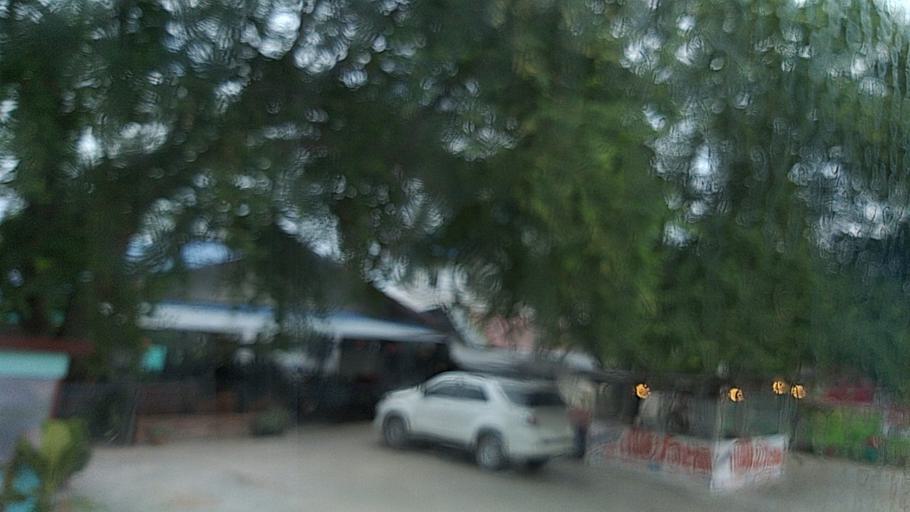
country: TH
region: Roi Et
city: Changhan
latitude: 16.1192
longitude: 103.4884
